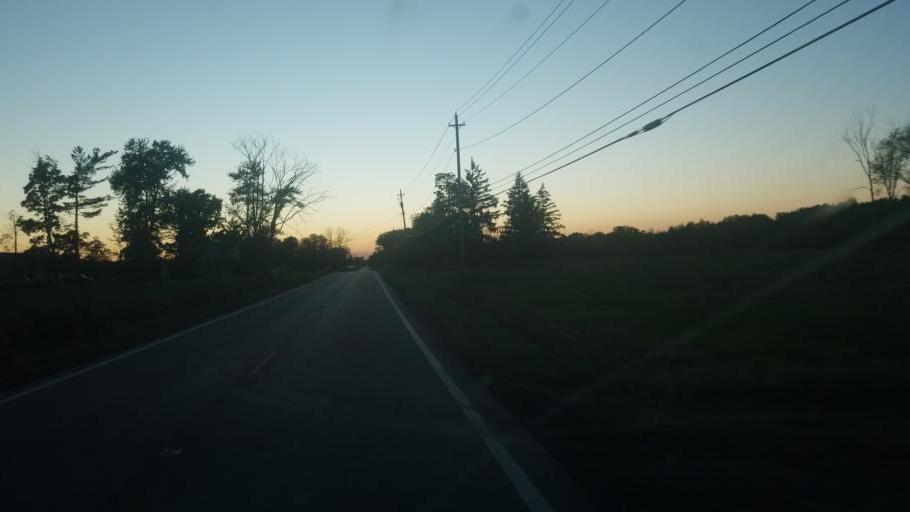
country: US
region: Ohio
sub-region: Ashtabula County
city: Andover
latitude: 41.7515
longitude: -80.5843
